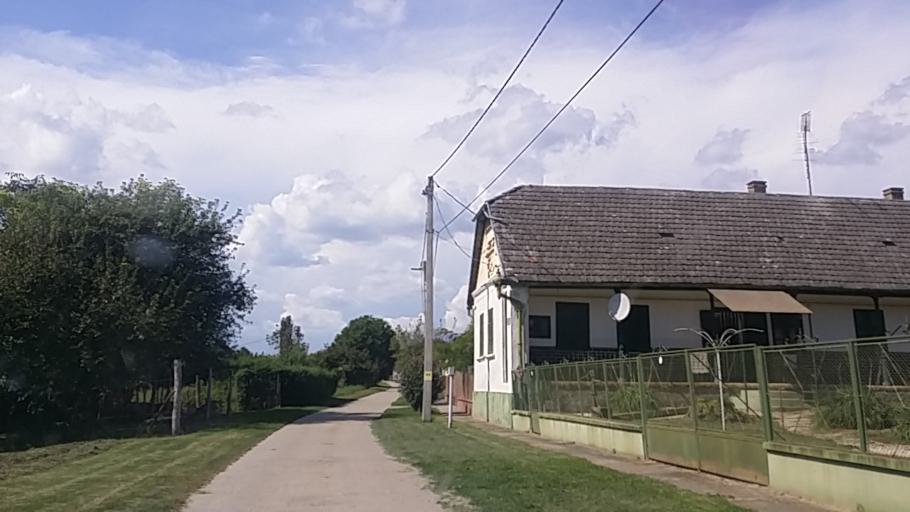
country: HU
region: Tolna
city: Gyonk
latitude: 46.5413
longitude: 18.4703
